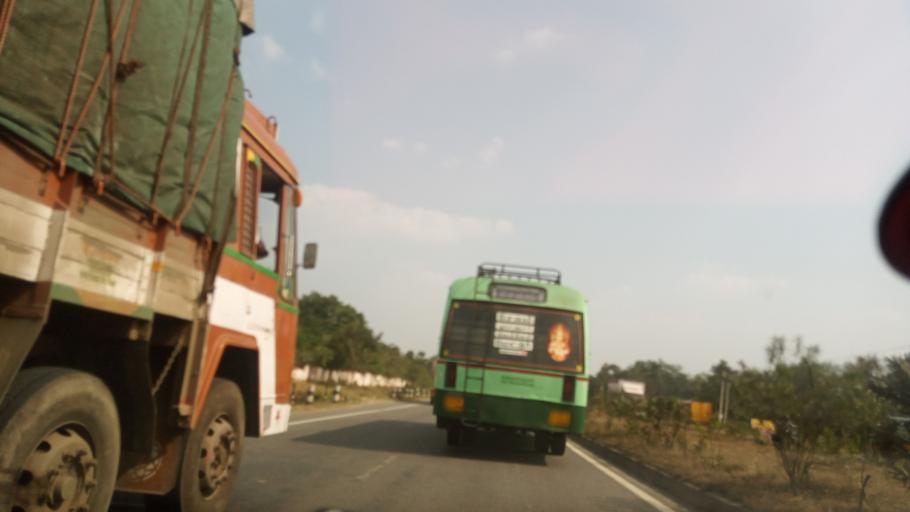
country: IN
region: Tamil Nadu
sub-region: Salem
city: Omalur
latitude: 11.7154
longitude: 78.0801
